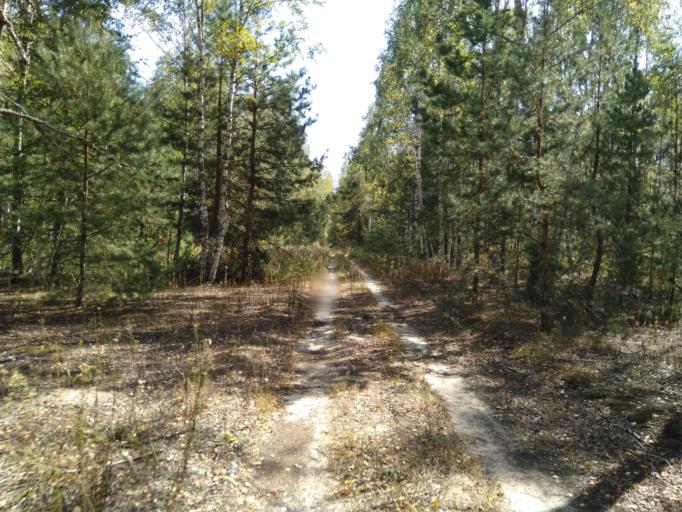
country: RU
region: Tambov
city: Rasskazovo
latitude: 52.7611
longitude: 41.8521
